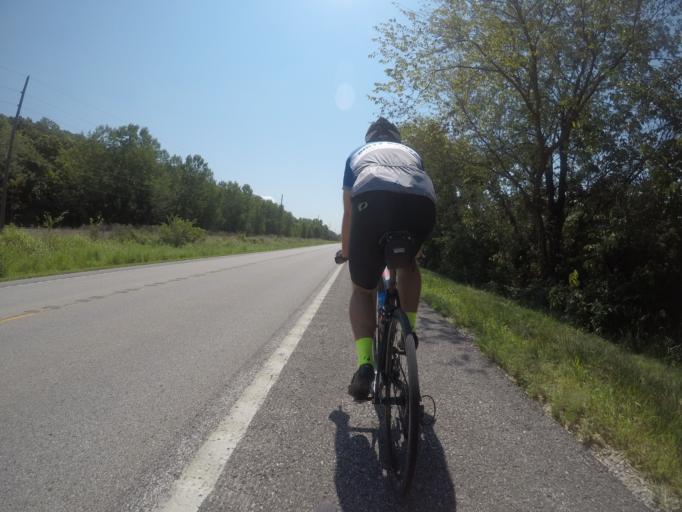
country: US
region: Missouri
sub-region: Platte County
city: Weston
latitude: 39.4880
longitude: -94.9960
